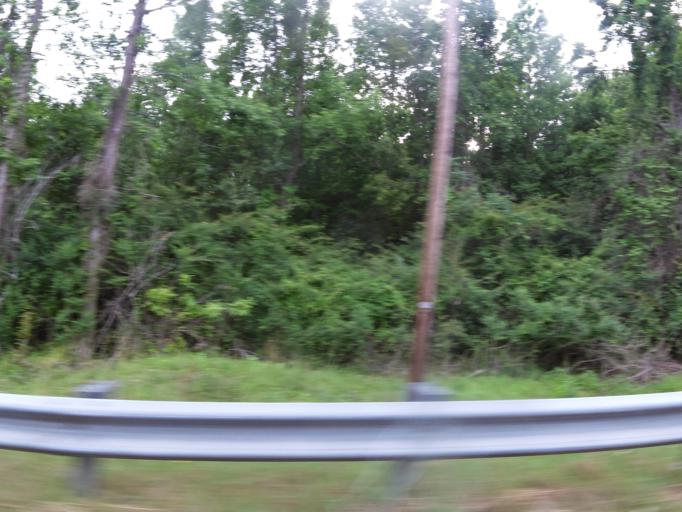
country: US
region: South Carolina
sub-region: Jasper County
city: Hardeeville
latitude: 32.2901
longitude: -81.0854
